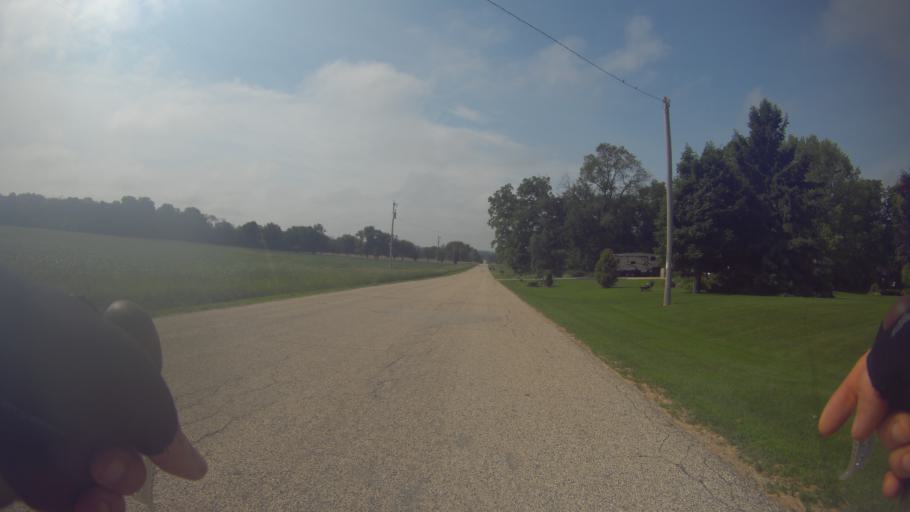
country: US
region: Wisconsin
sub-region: Dane County
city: Stoughton
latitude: 42.9617
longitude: -89.1810
